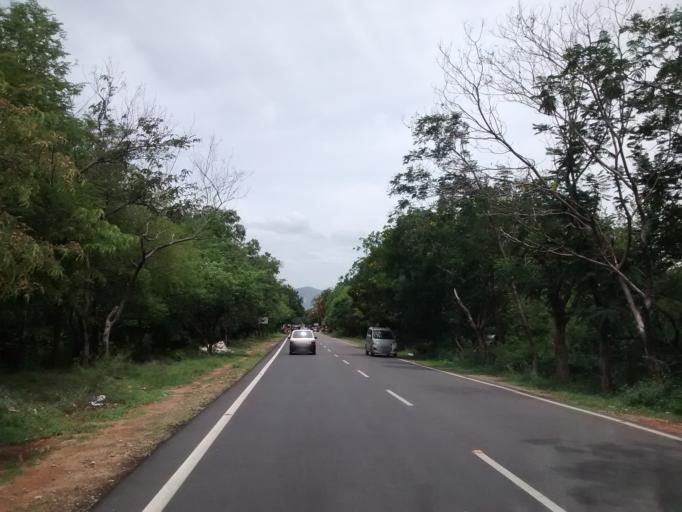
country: IN
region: Andhra Pradesh
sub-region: Chittoor
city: Tirupati
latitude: 13.6261
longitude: 79.3671
